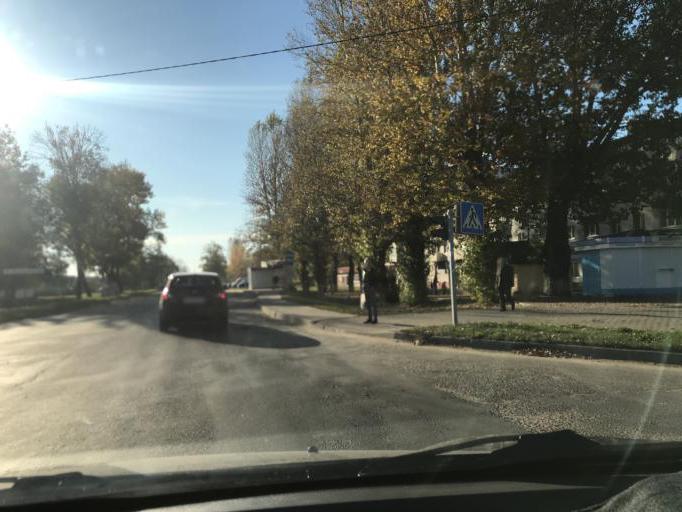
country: BY
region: Minsk
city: Slutsk
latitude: 53.0421
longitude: 27.5891
